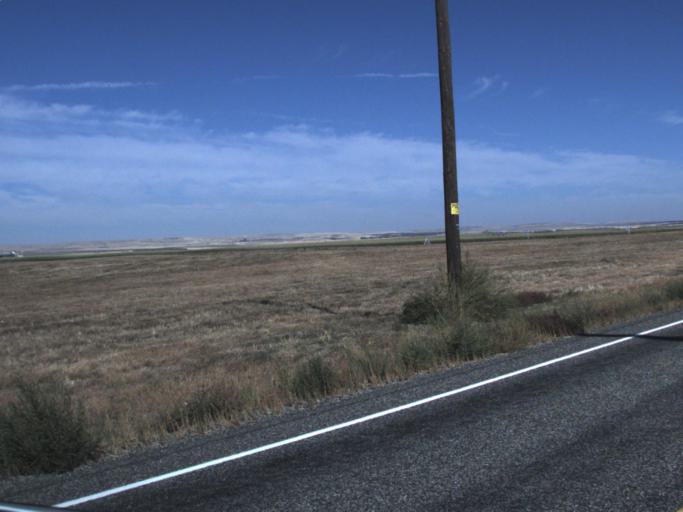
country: US
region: Washington
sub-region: Walla Walla County
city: Burbank
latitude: 46.2427
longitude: -118.8246
